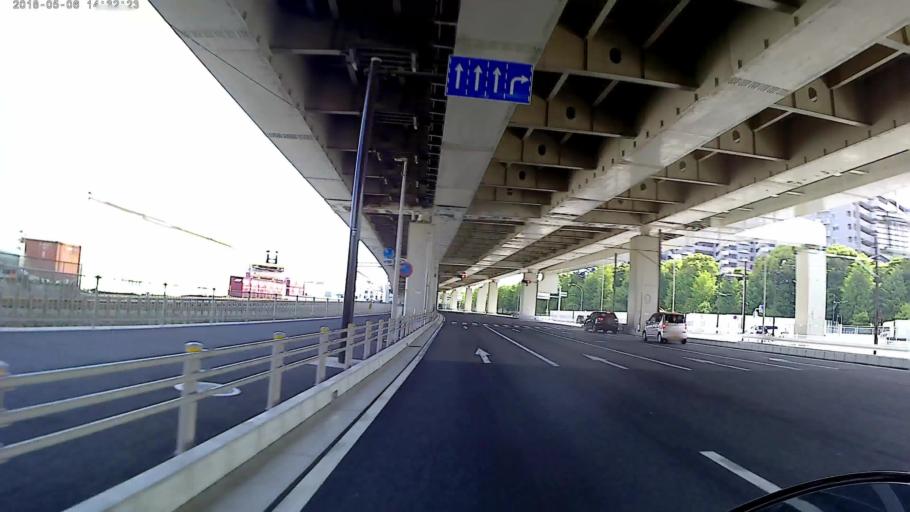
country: JP
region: Kanagawa
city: Yokohama
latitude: 35.4258
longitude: 139.6710
